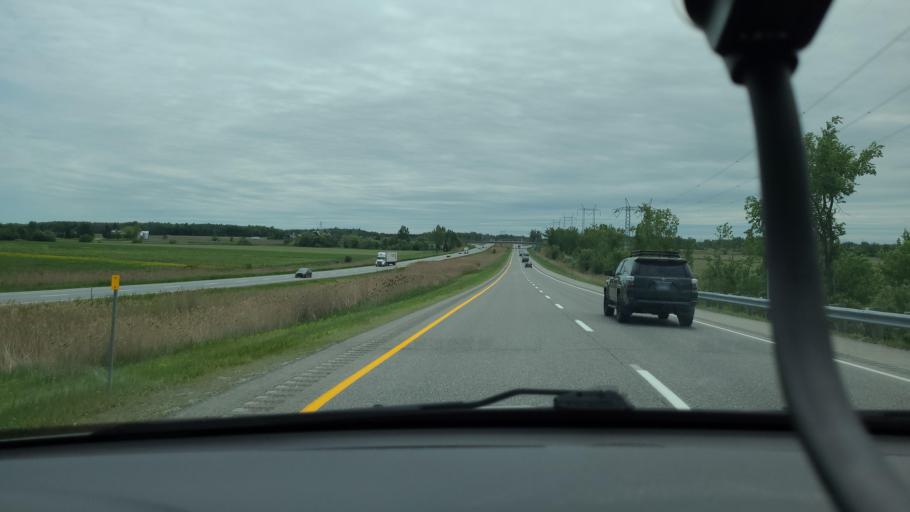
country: CA
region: Quebec
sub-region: Lanaudiere
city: Mascouche
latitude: 45.7965
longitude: -73.5844
